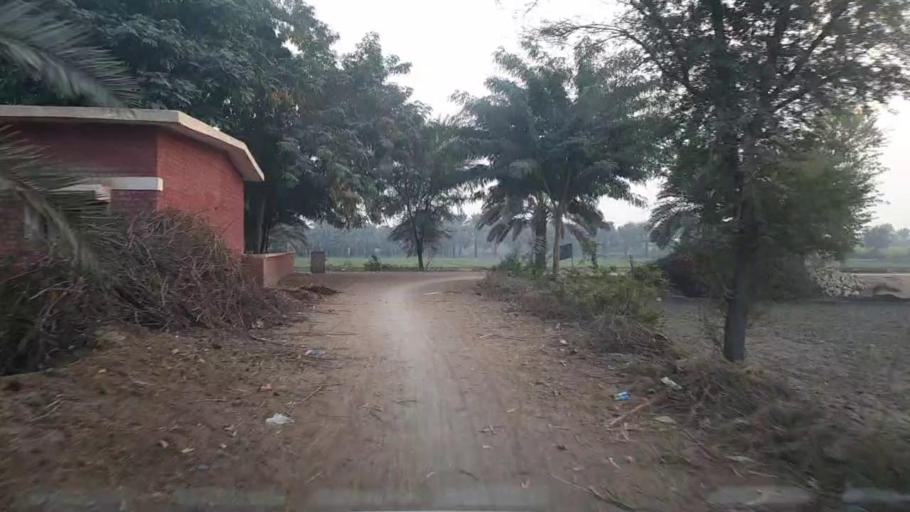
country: PK
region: Sindh
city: Kot Diji
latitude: 27.3380
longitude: 68.6407
